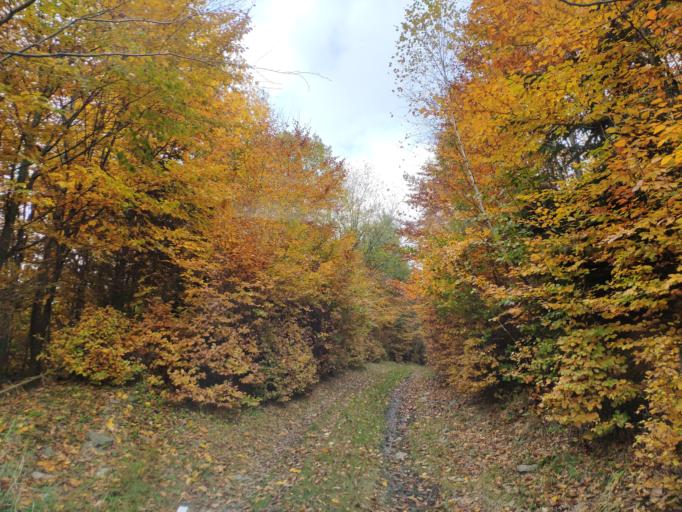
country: SK
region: Kosicky
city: Medzev
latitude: 48.7368
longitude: 20.9935
